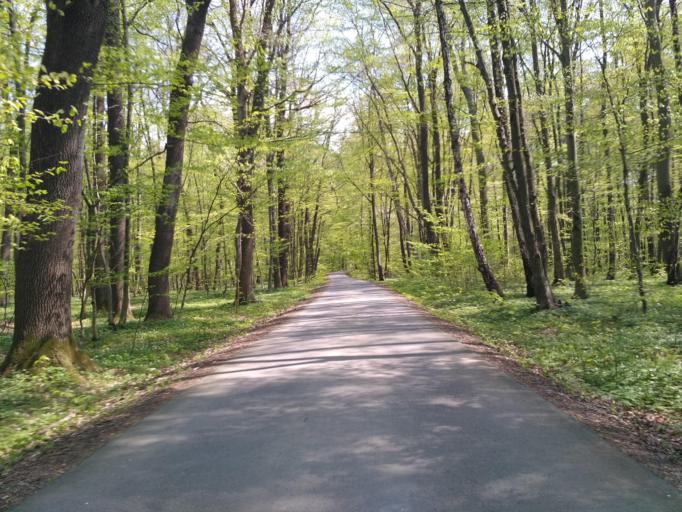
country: PL
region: Subcarpathian Voivodeship
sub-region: Powiat jasielski
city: Tarnowiec
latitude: 49.7400
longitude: 21.5942
